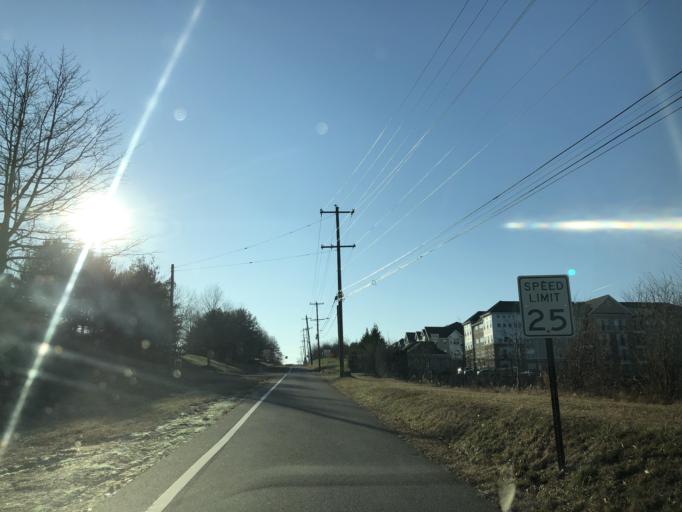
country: US
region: Pennsylvania
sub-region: Delaware County
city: Chester Heights
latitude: 39.8806
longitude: -75.5195
